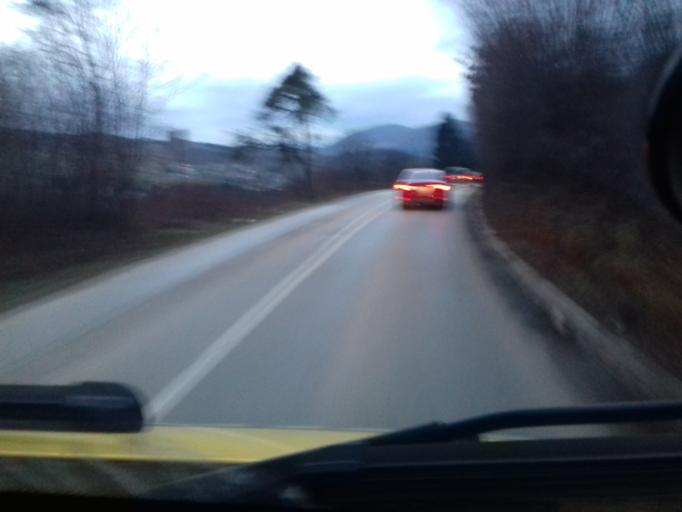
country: BA
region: Federation of Bosnia and Herzegovina
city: Visoko
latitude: 43.9966
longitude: 18.2091
